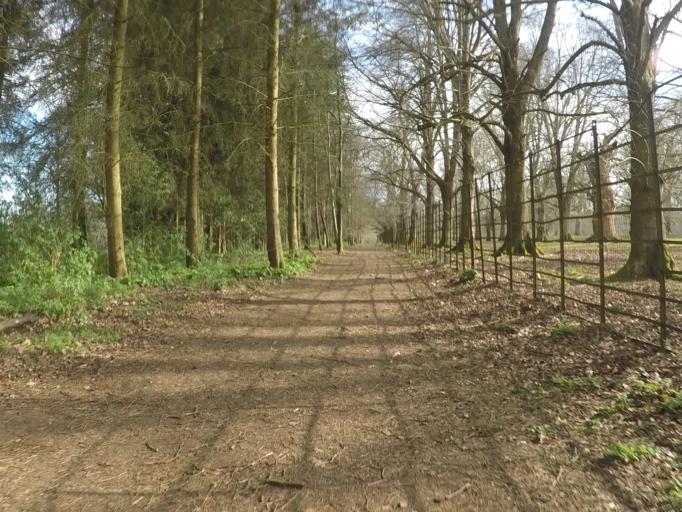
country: GB
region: England
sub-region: Oxfordshire
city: Charlbury
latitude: 51.8624
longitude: -1.4845
